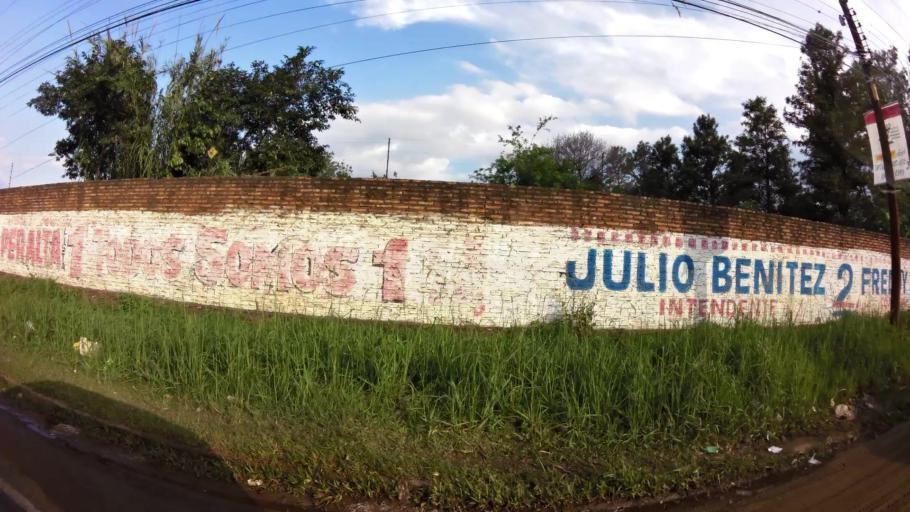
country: PY
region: Central
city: Fernando de la Mora
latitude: -25.3476
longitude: -57.5281
